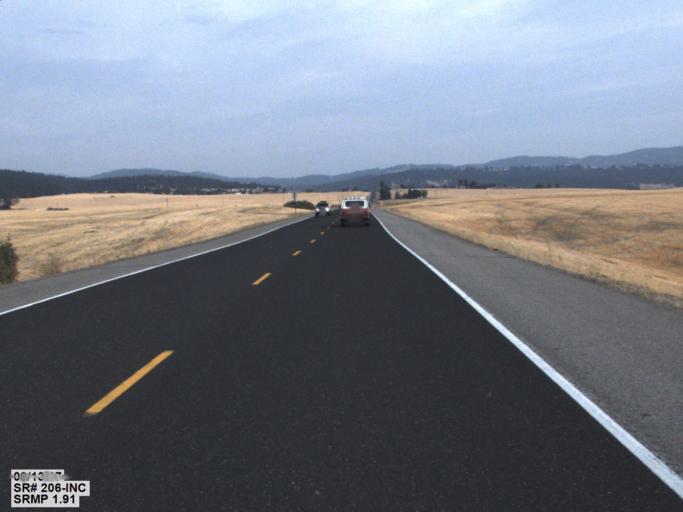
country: US
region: Washington
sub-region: Spokane County
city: Mead
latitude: 47.7875
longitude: -117.3140
